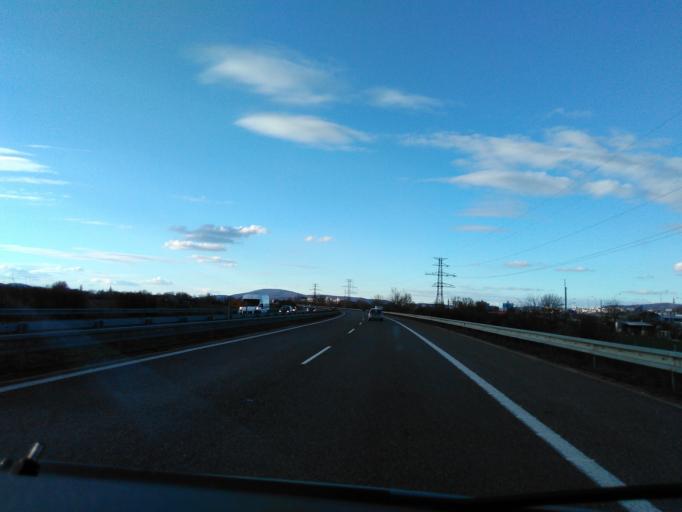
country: AT
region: Burgenland
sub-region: Politischer Bezirk Neusiedl am See
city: Kittsee
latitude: 48.1004
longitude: 17.0966
